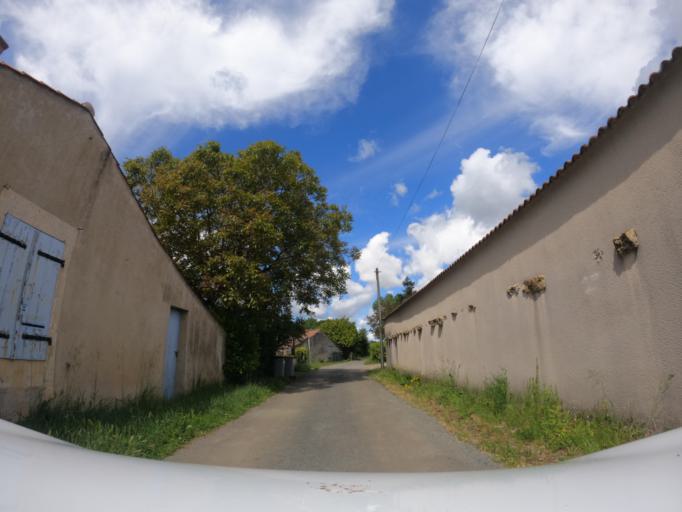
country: FR
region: Pays de la Loire
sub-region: Departement de la Vendee
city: Le Champ-Saint-Pere
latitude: 46.4914
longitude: -1.3201
